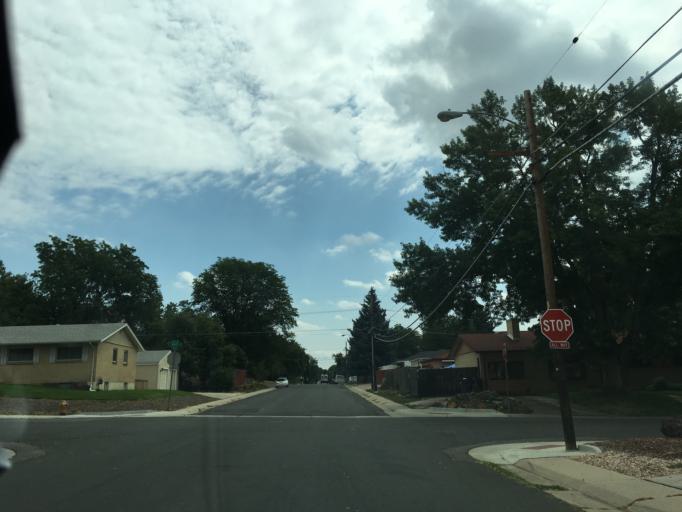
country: US
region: Colorado
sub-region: Arapahoe County
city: Sheridan
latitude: 39.6626
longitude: -105.0495
